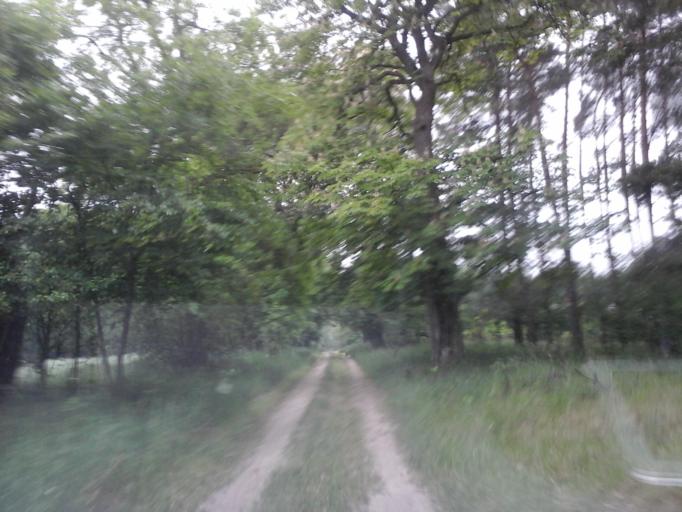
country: PL
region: West Pomeranian Voivodeship
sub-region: Powiat choszczenski
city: Pelczyce
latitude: 52.9753
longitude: 15.3713
